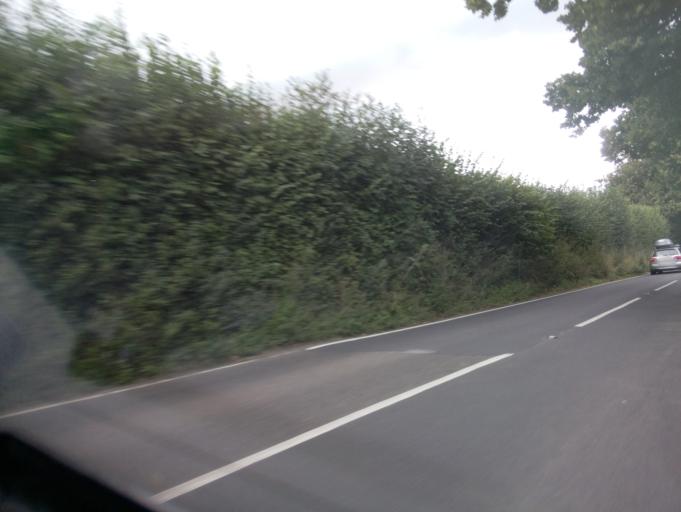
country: GB
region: England
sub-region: Devon
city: Exminster
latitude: 50.6681
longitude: -3.4832
